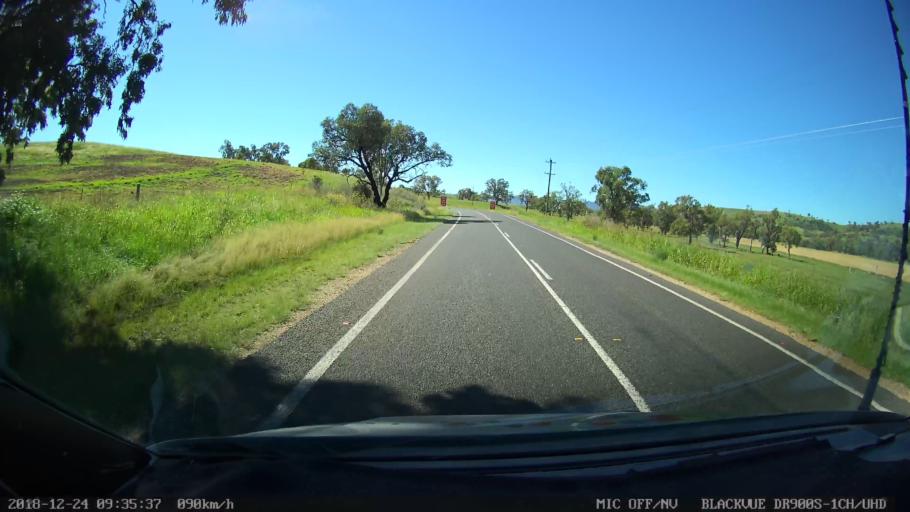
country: AU
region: New South Wales
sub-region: Liverpool Plains
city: Quirindi
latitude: -31.6316
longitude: 150.7185
